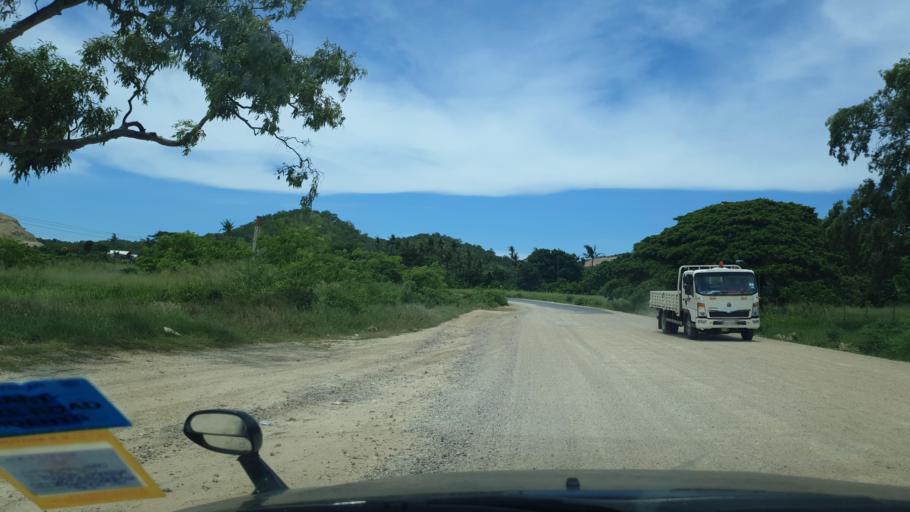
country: PG
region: National Capital
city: Port Moresby
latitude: -9.4249
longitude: 147.0744
